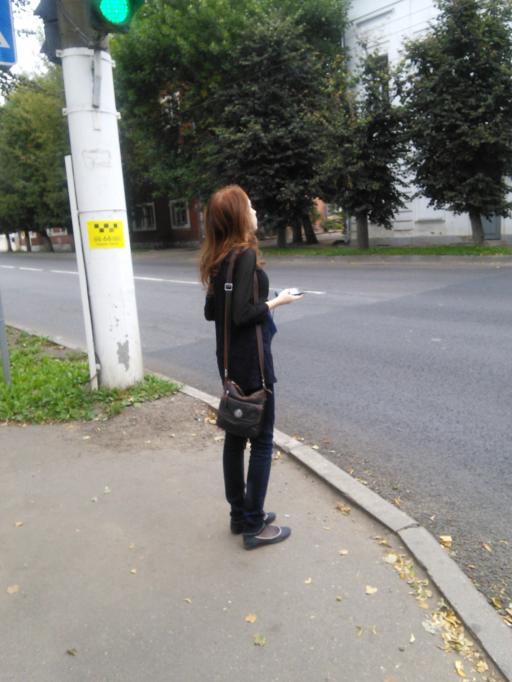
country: RU
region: Kostroma
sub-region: Kostromskoy Rayon
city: Kostroma
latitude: 57.7708
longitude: 40.9328
